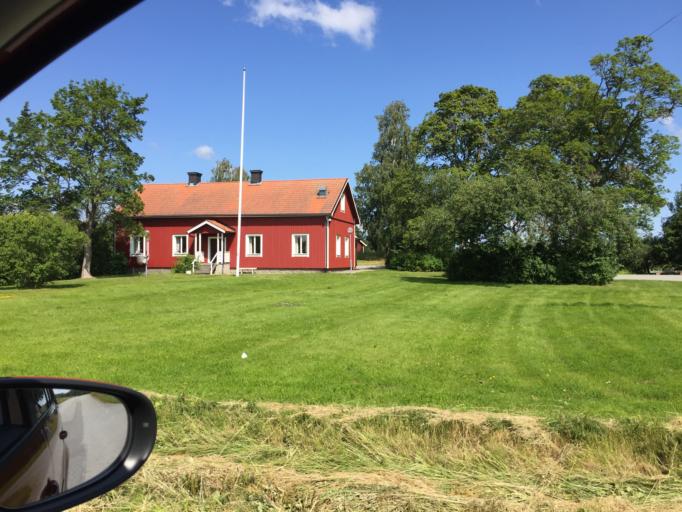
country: SE
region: Uppsala
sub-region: Enkopings Kommun
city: Hummelsta
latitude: 59.5861
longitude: 16.9283
